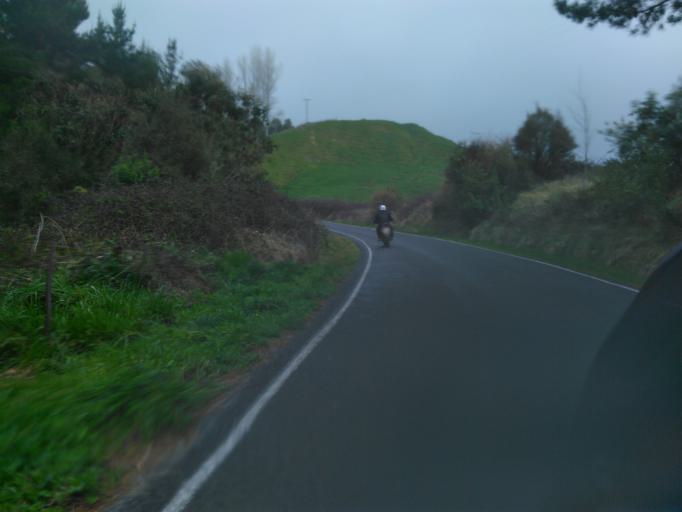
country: NZ
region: Gisborne
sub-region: Gisborne District
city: Gisborne
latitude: -38.6651
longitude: 177.7160
